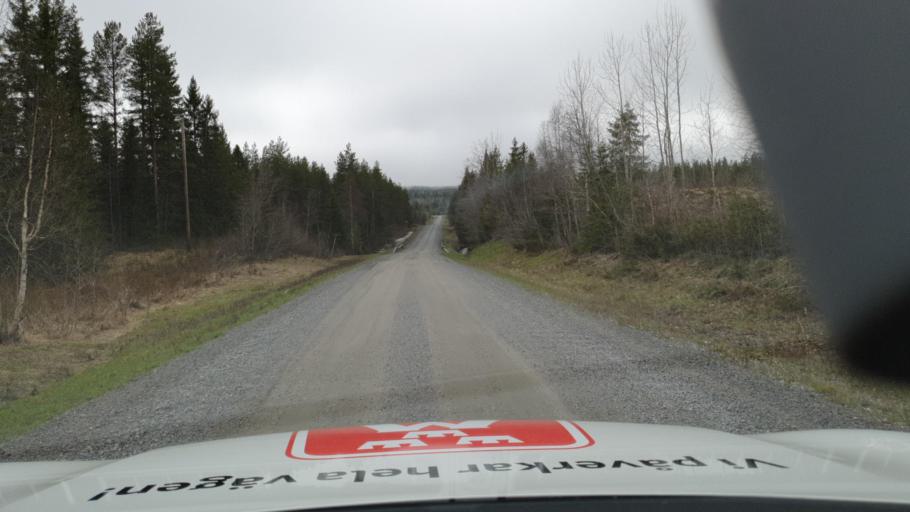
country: SE
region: Vaesterbotten
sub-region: Bjurholms Kommun
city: Bjurholm
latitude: 63.7923
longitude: 19.3220
